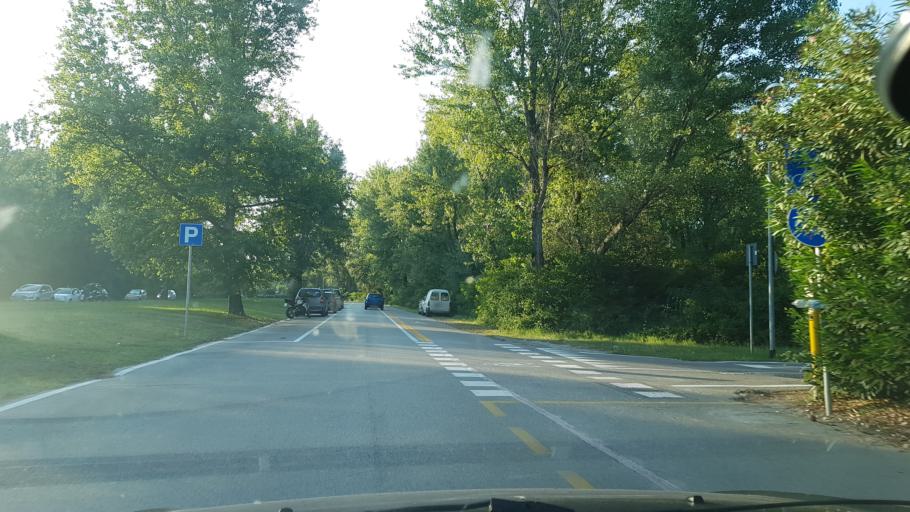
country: IT
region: Friuli Venezia Giulia
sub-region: Provincia di Gorizia
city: Monfalcone
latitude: 45.7773
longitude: 13.5265
